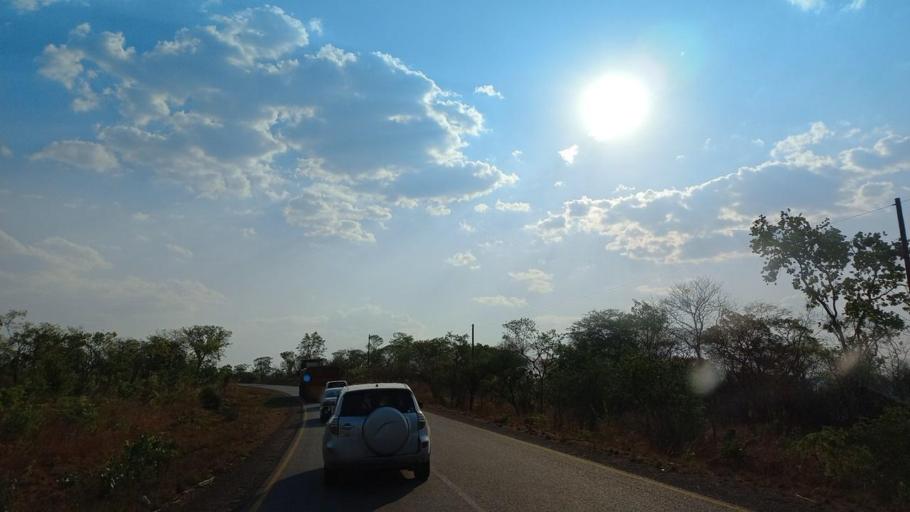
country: ZM
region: Lusaka
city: Luangwa
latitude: -14.9789
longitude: 29.9923
